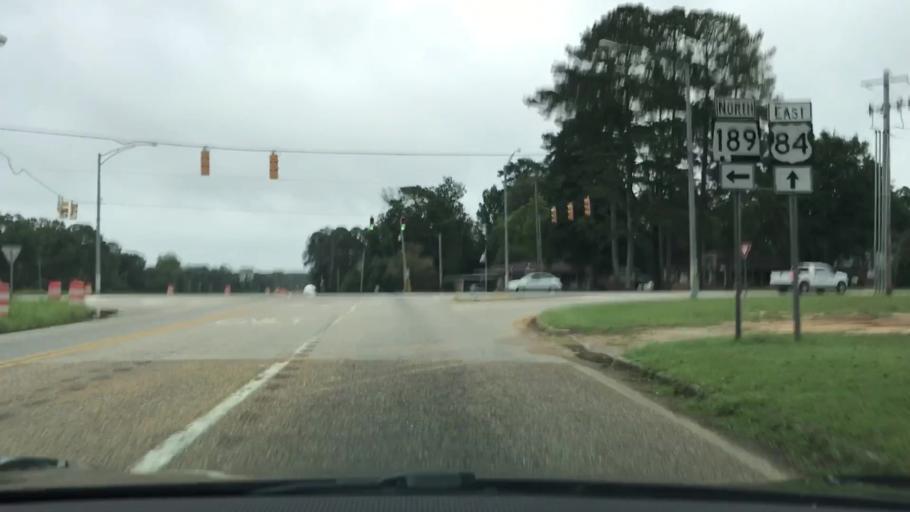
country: US
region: Alabama
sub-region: Coffee County
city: Elba
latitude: 31.4260
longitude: -86.0747
